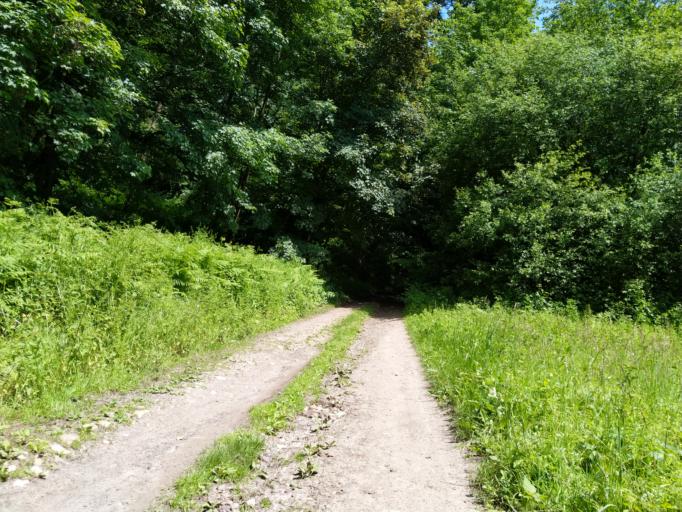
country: BE
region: Wallonia
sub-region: Province du Hainaut
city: Roeulx
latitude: 50.5003
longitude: 4.0258
